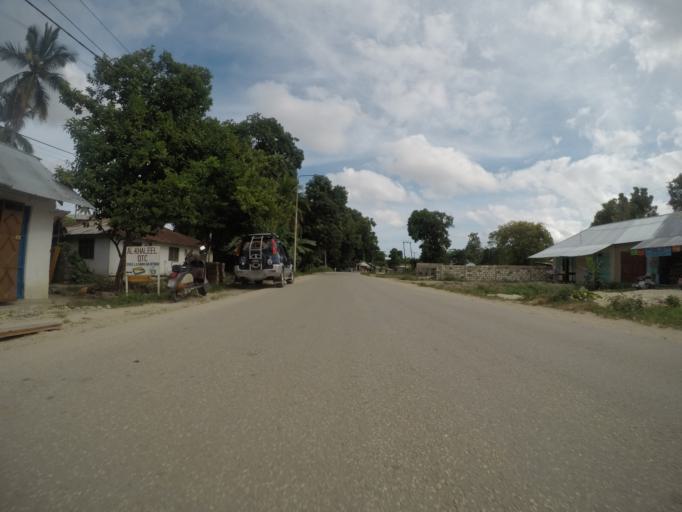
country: TZ
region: Pemba South
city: Chake Chake
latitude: -5.2401
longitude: 39.7812
